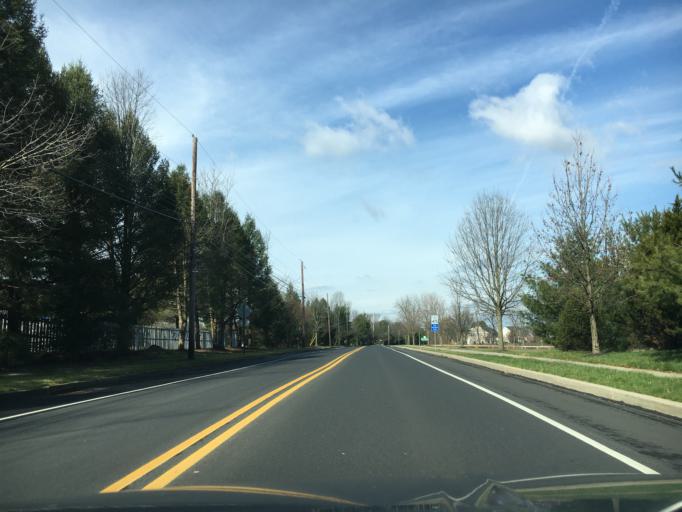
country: US
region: Pennsylvania
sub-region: Northampton County
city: Bath
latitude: 40.6816
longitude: -75.4015
